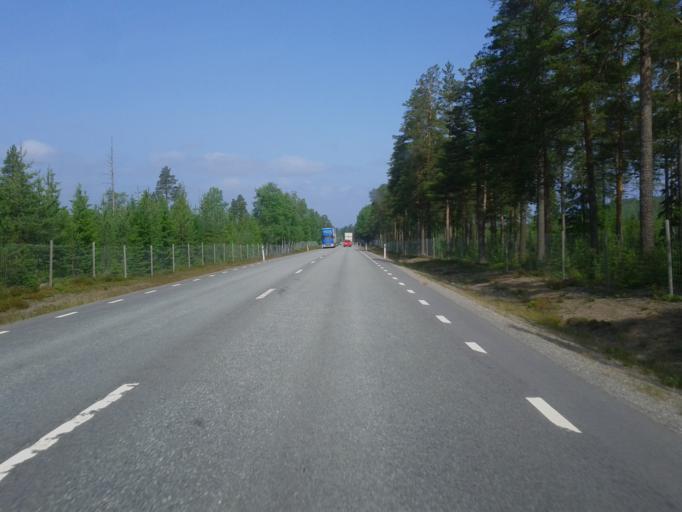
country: SE
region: Vaesterbotten
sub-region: Skelleftea Kommun
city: Burea
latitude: 64.5793
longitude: 21.2217
